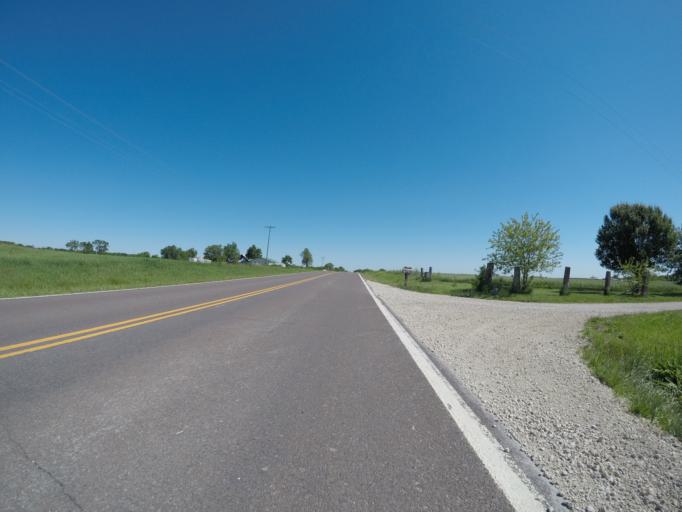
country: US
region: Kansas
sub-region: Wabaunsee County
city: Alma
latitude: 38.8154
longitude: -96.0947
